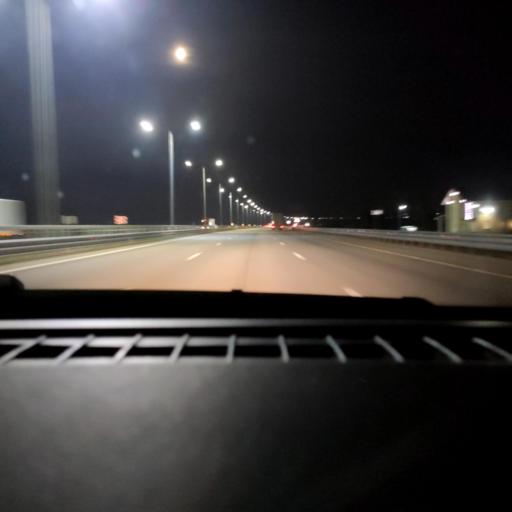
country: RU
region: Voronezj
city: Somovo
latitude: 51.7814
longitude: 39.2935
